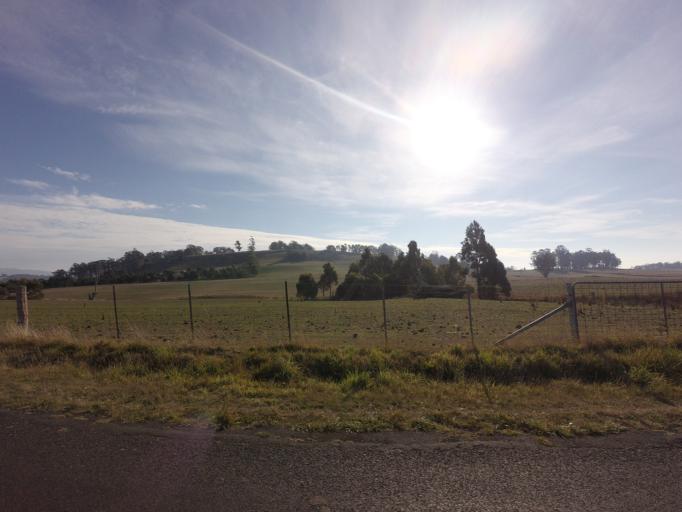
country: AU
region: Tasmania
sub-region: Sorell
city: Sorell
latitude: -42.4808
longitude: 147.4563
